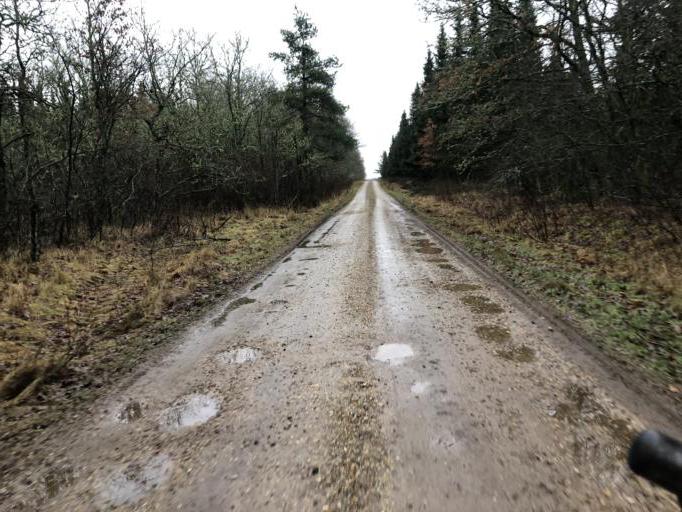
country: DK
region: Central Jutland
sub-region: Holstebro Kommune
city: Ulfborg
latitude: 56.2903
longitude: 8.4567
